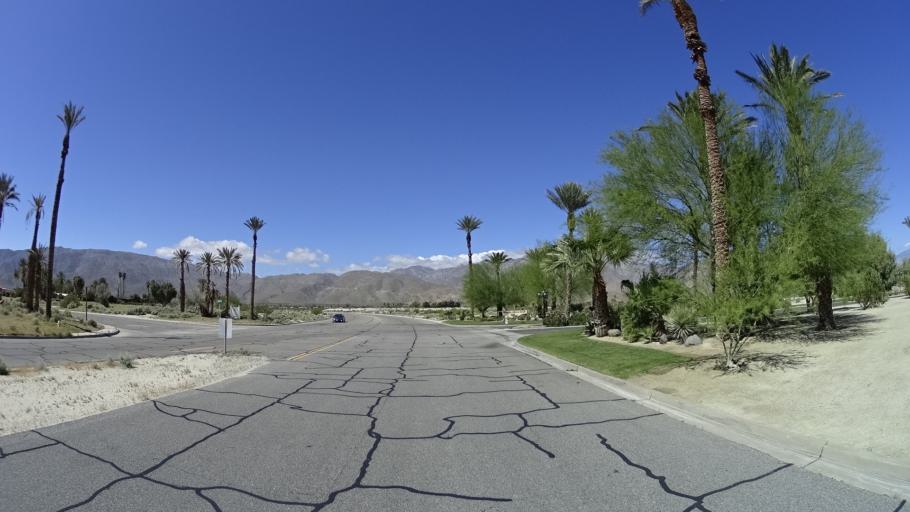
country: US
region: California
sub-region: San Diego County
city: Borrego Springs
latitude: 33.2354
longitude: -116.3559
